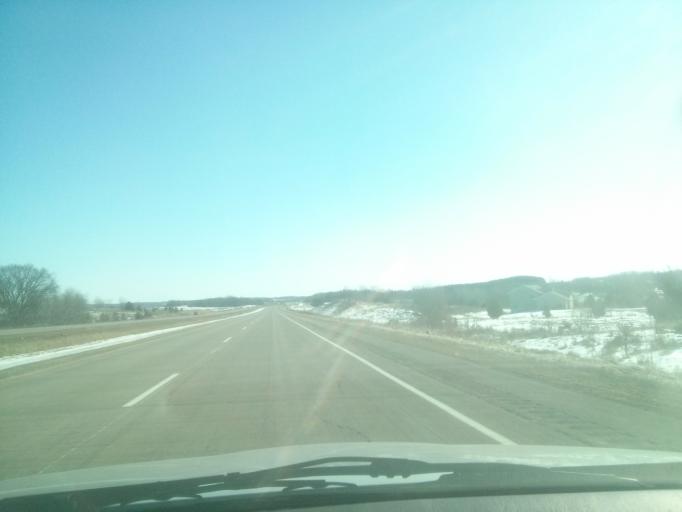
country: US
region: Wisconsin
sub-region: Saint Croix County
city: Somerset
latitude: 45.1085
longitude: -92.6952
